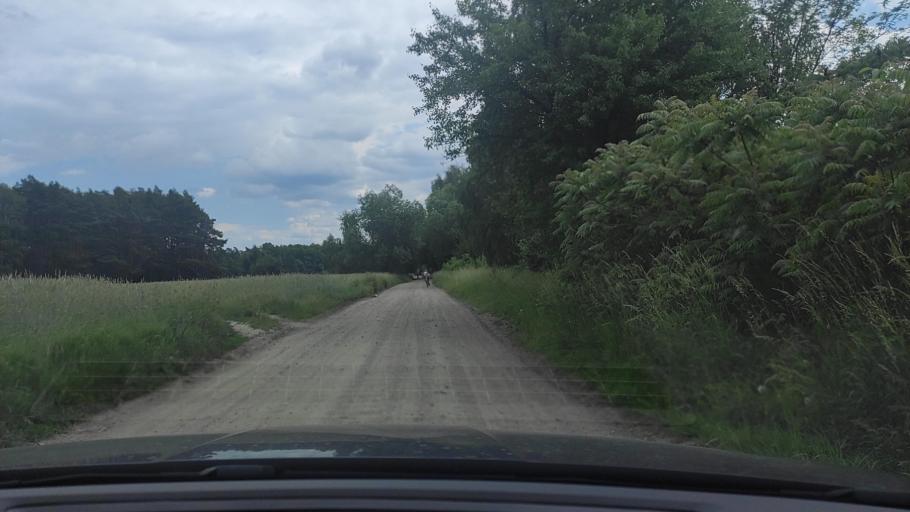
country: PL
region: Greater Poland Voivodeship
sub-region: Powiat poznanski
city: Pobiedziska
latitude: 52.4947
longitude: 17.1916
